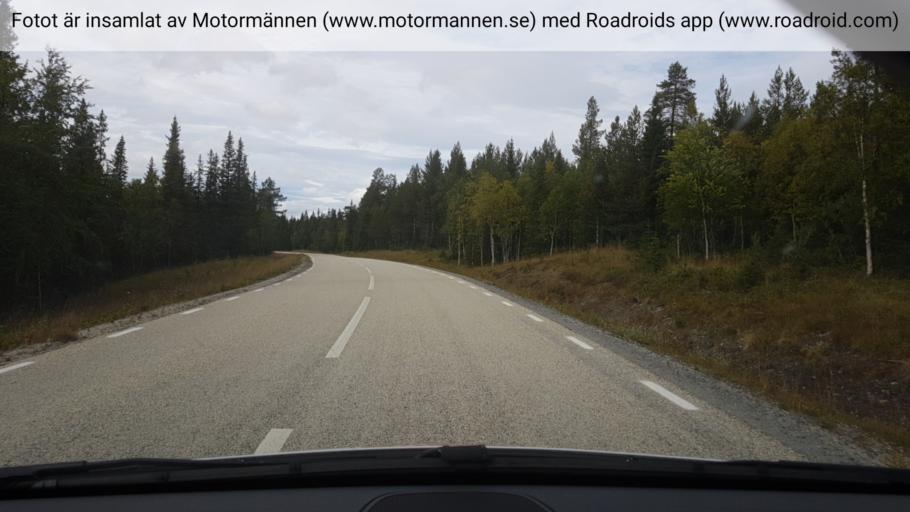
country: SE
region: Jaemtland
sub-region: Are Kommun
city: Are
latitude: 62.8343
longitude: 12.8459
